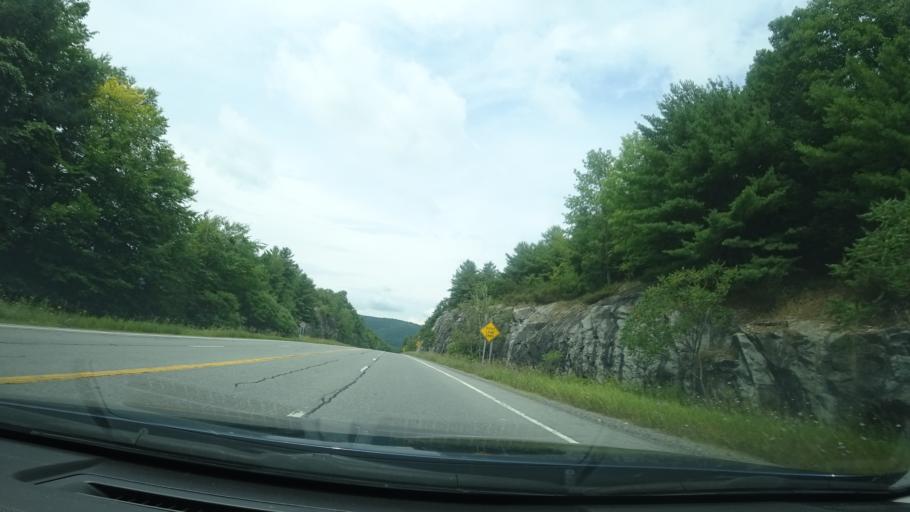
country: US
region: New York
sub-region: Washington County
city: Whitehall
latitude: 43.6919
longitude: -73.4242
